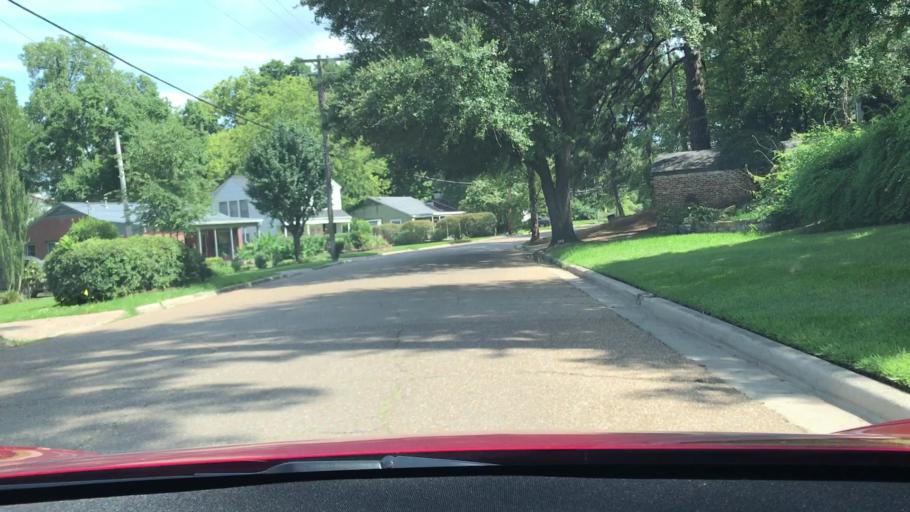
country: US
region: Louisiana
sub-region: Bossier Parish
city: Bossier City
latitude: 32.4803
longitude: -93.7315
